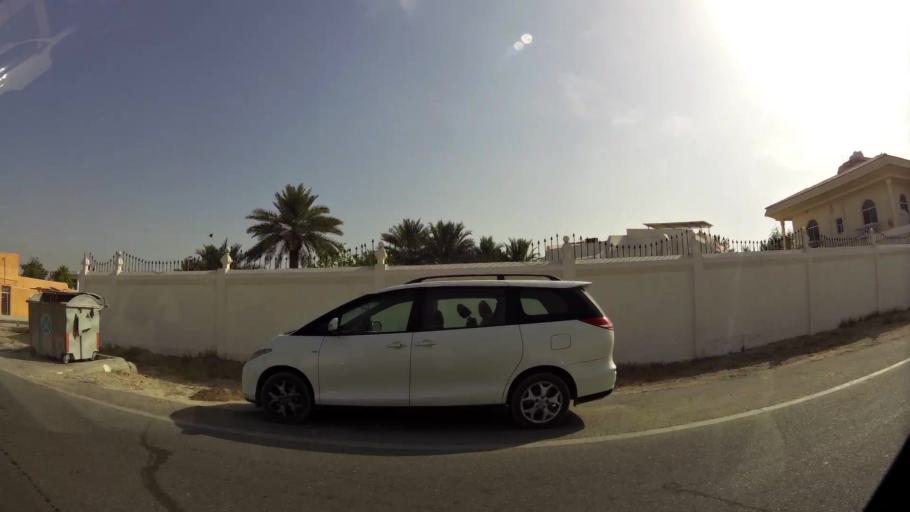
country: AE
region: Ash Shariqah
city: Sharjah
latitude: 25.2260
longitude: 55.4007
